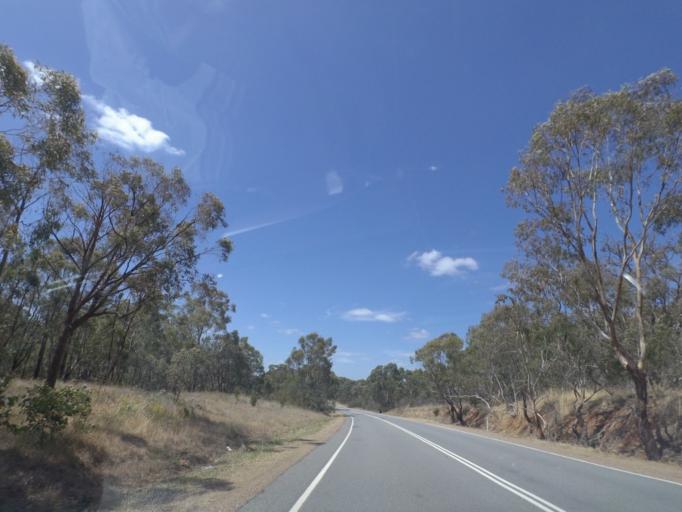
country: AU
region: Victoria
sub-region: Wangaratta
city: Wangaratta
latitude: -36.4605
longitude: 146.2333
